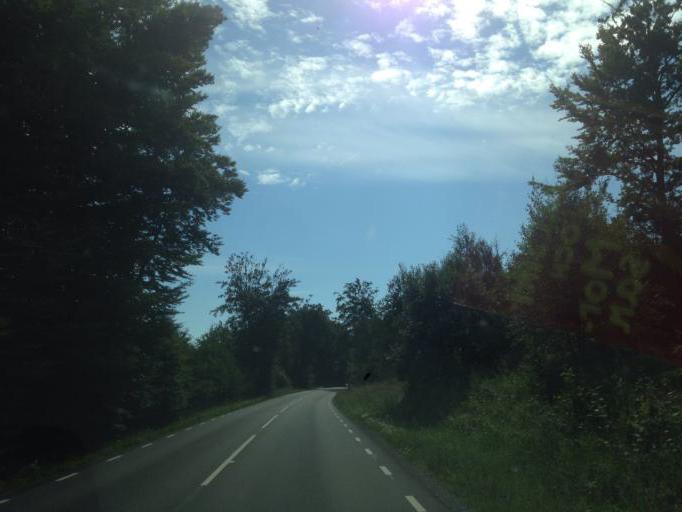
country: SE
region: Skane
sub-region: Tomelilla Kommun
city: Tomelilla
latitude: 55.6352
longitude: 14.0866
